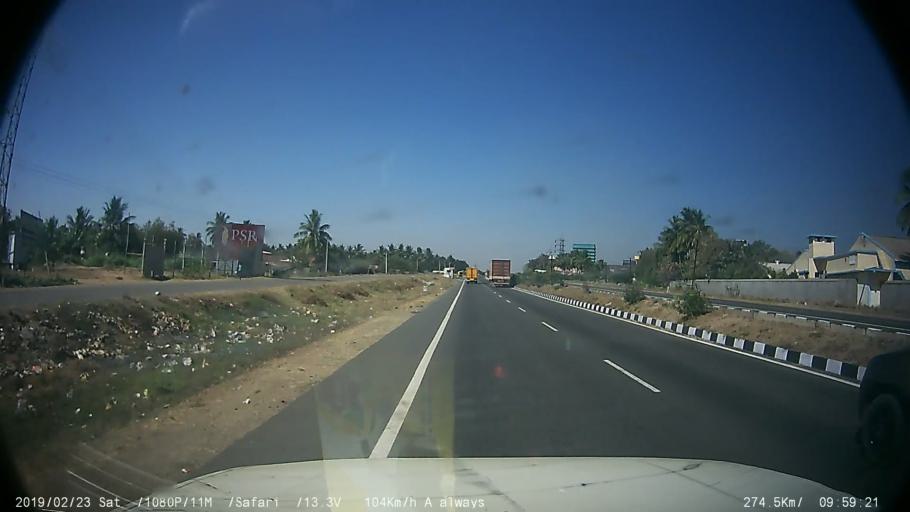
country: IN
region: Tamil Nadu
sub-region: Erode
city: Vijayapuri
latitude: 11.2343
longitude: 77.4819
